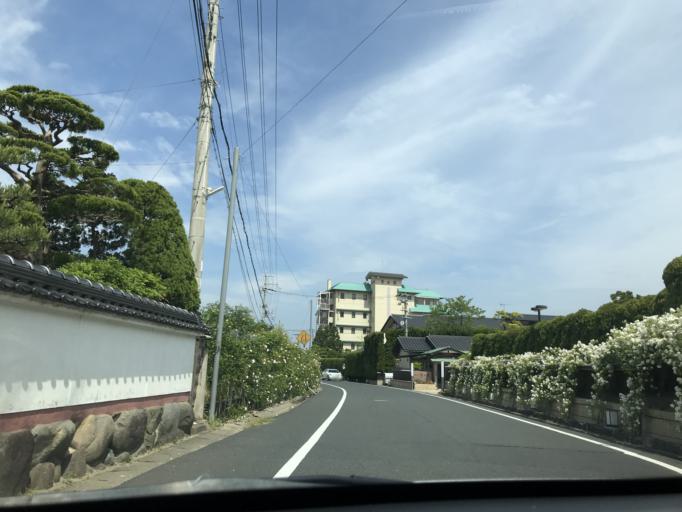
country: JP
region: Hyogo
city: Toyooka
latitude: 35.6586
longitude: 134.9652
